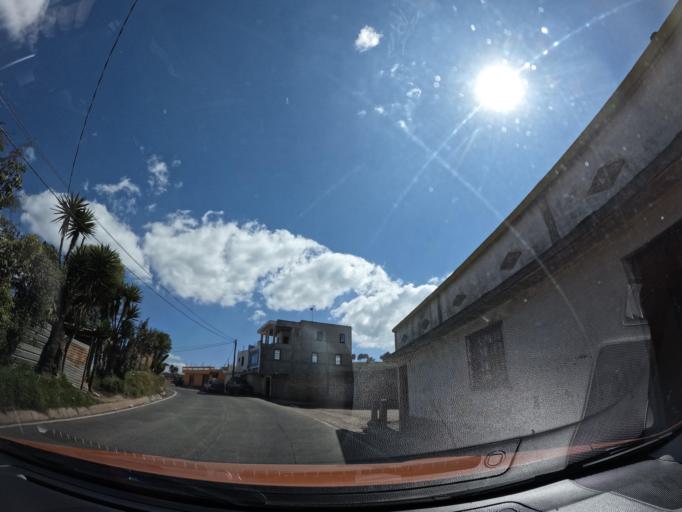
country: GT
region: Chimaltenango
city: Patzun
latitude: 14.6548
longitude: -91.0551
